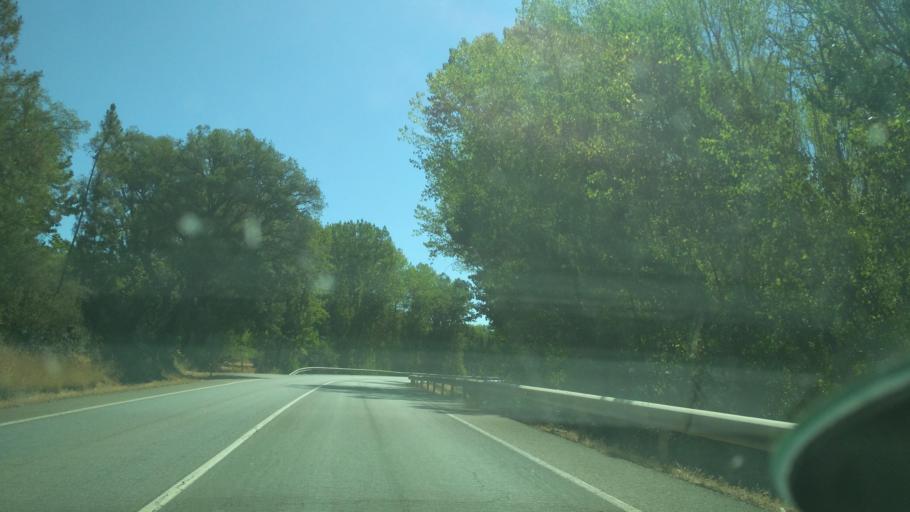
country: ES
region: Andalusia
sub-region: Provincia de Huelva
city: Fuenteheridos
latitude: 37.9166
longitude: -6.6818
